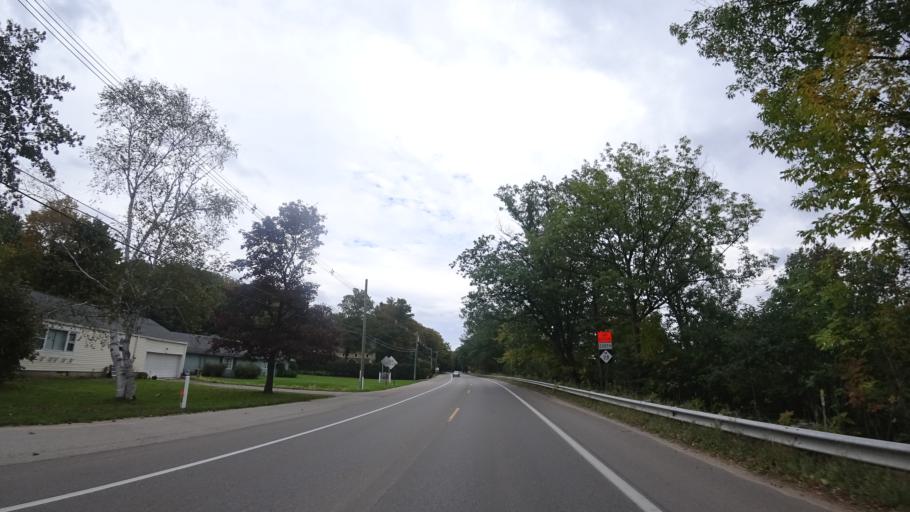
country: US
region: Michigan
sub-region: Emmet County
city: Harbor Springs
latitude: 45.4319
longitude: -84.9683
